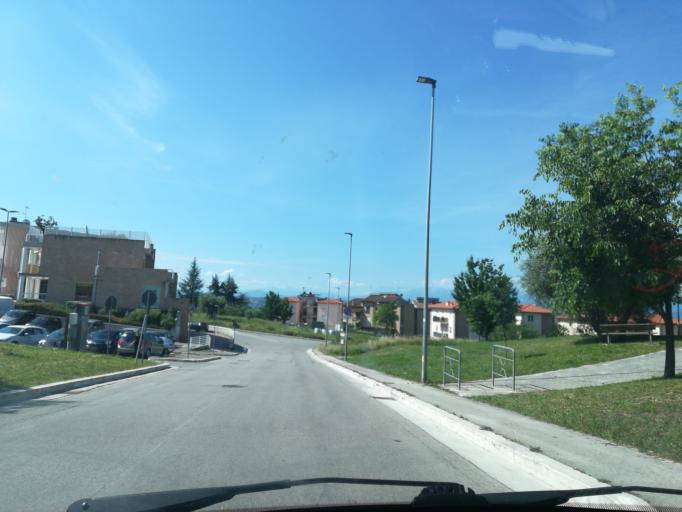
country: IT
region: The Marches
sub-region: Provincia di Macerata
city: Macerata
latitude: 43.2921
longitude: 13.4722
